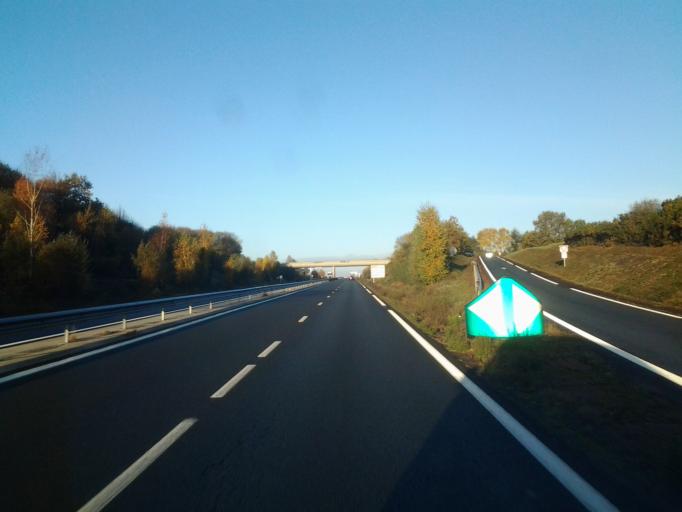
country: FR
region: Pays de la Loire
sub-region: Departement de la Vendee
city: La Chaize-le-Vicomte
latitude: 46.6668
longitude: -1.3002
